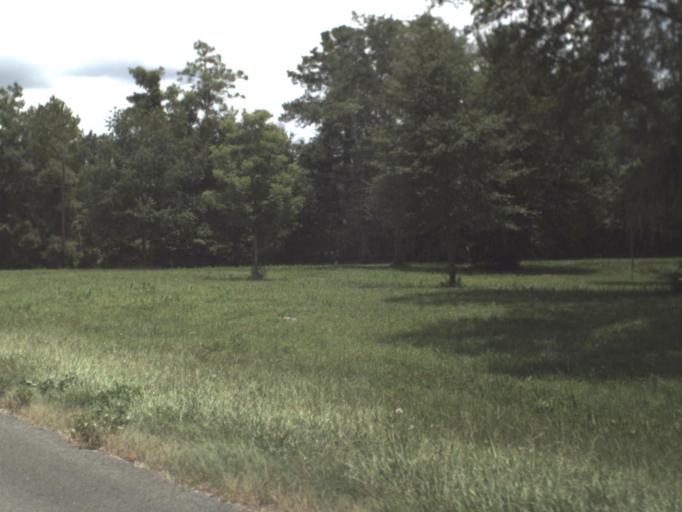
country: US
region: Florida
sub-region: Taylor County
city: Perry
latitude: 30.1009
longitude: -83.6182
